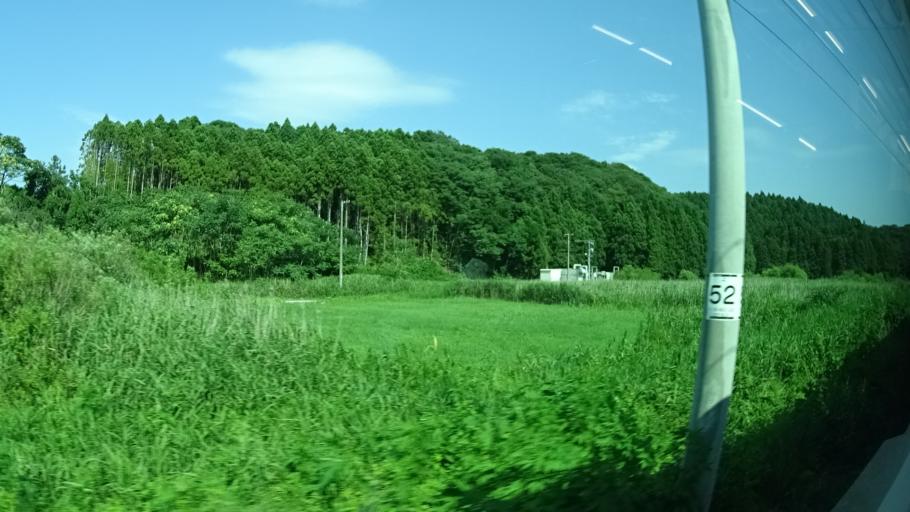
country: JP
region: Miyagi
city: Kogota
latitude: 38.4973
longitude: 141.0866
